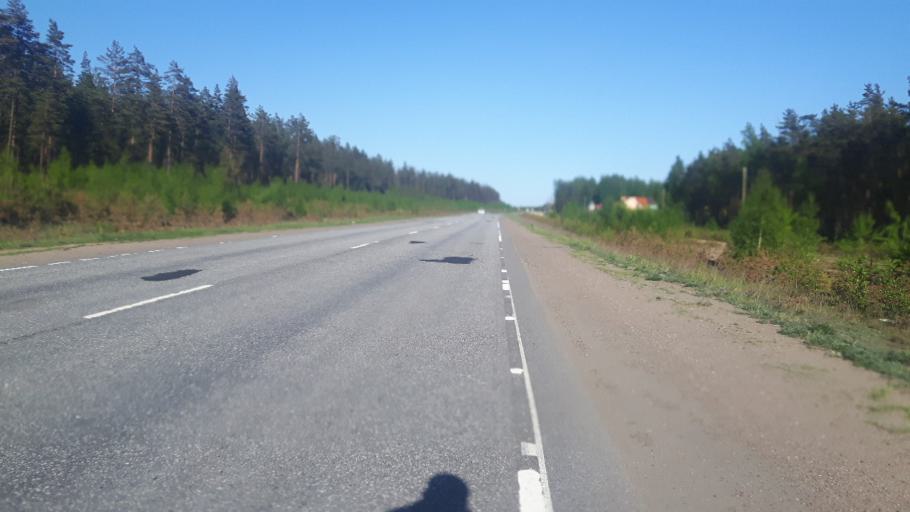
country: RU
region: Leningrad
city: Sosnovyy Bor
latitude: 60.1694
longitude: 29.2020
